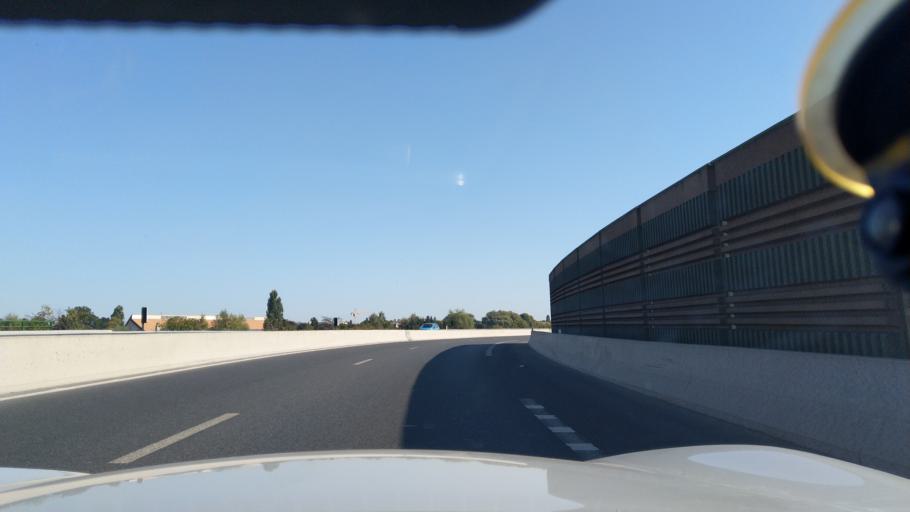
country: FR
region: Ile-de-France
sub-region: Departement du Val-d'Oise
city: Arnouville
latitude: 48.9753
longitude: 2.4268
